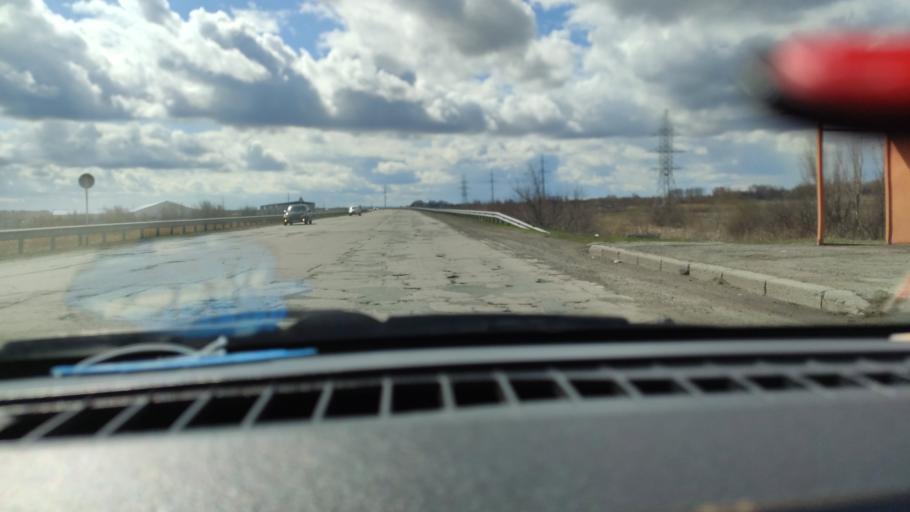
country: RU
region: Samara
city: Tol'yatti
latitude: 53.6706
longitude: 49.4144
